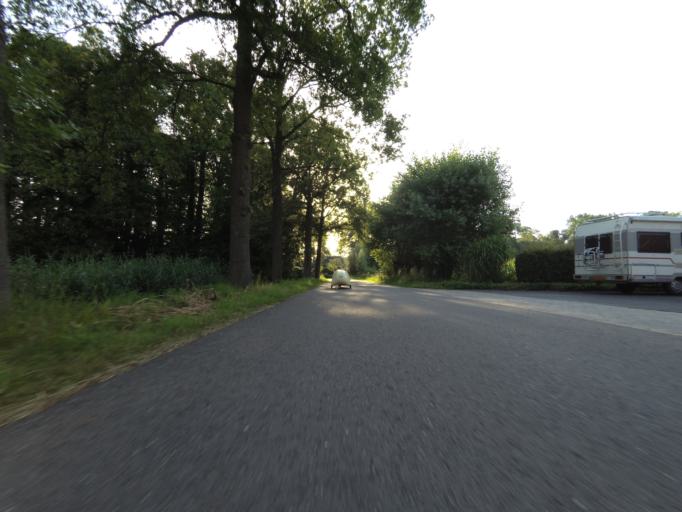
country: NL
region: Gelderland
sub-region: Gemeente Voorst
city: Twello
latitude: 52.2484
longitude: 6.1093
